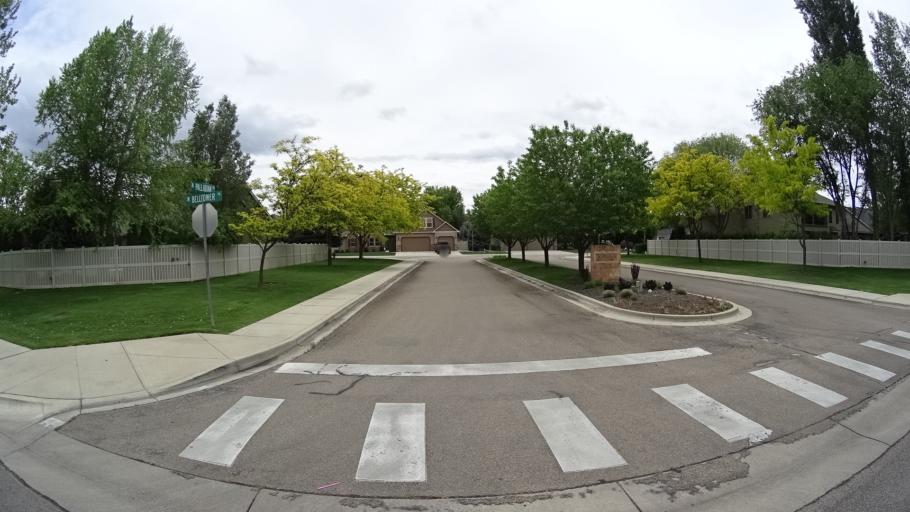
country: US
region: Idaho
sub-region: Ada County
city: Meridian
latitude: 43.6431
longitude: -116.4254
